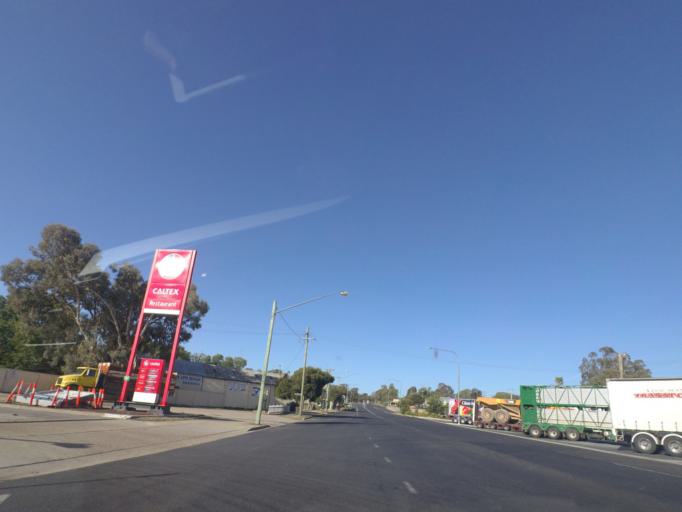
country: AU
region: New South Wales
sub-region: Wagga Wagga
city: Forest Hill
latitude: -35.2774
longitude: 147.7364
